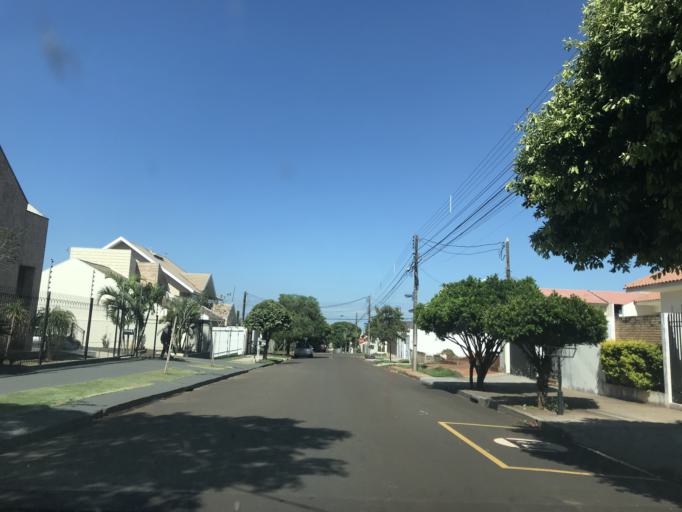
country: BR
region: Parana
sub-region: Maringa
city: Maringa
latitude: -23.4491
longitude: -51.9583
